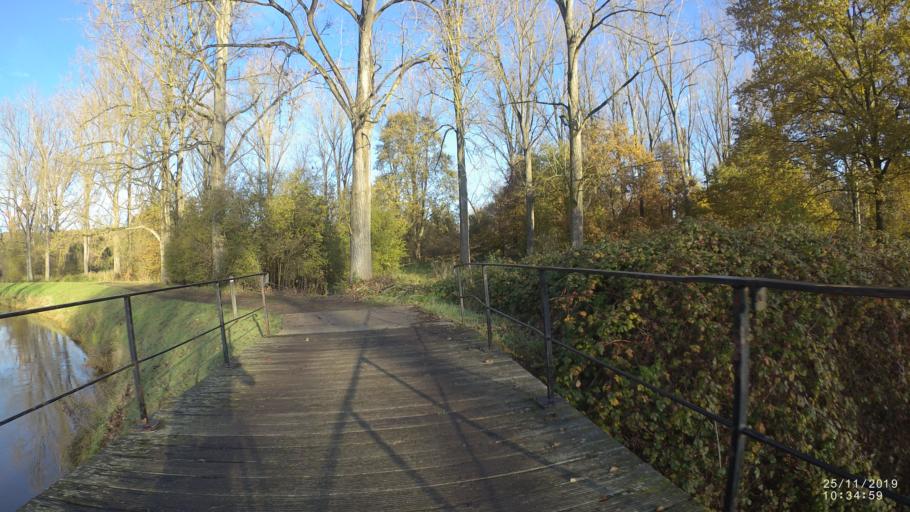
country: BE
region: Flanders
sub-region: Provincie Vlaams-Brabant
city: Scherpenheuvel-Zichem
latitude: 51.0071
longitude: 4.9663
